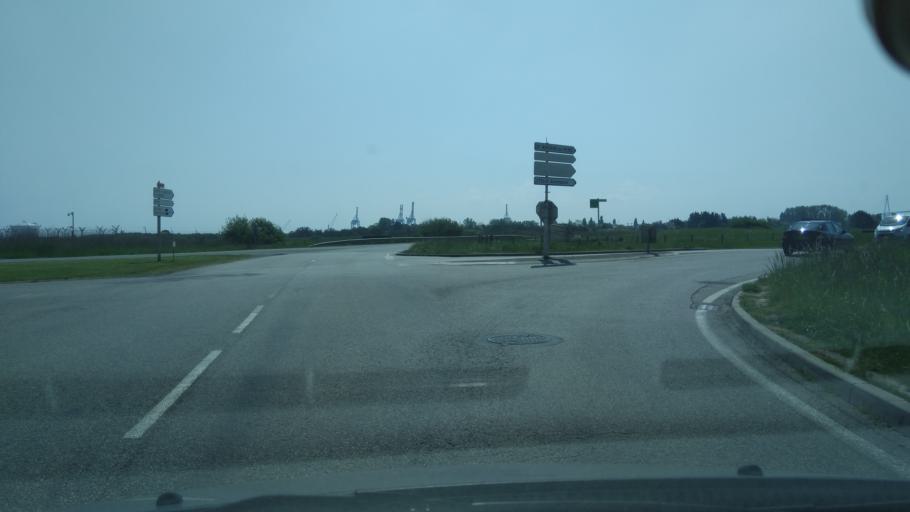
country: FR
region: Pays de la Loire
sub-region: Departement de la Loire-Atlantique
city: Trignac
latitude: 47.3098
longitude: -2.1734
